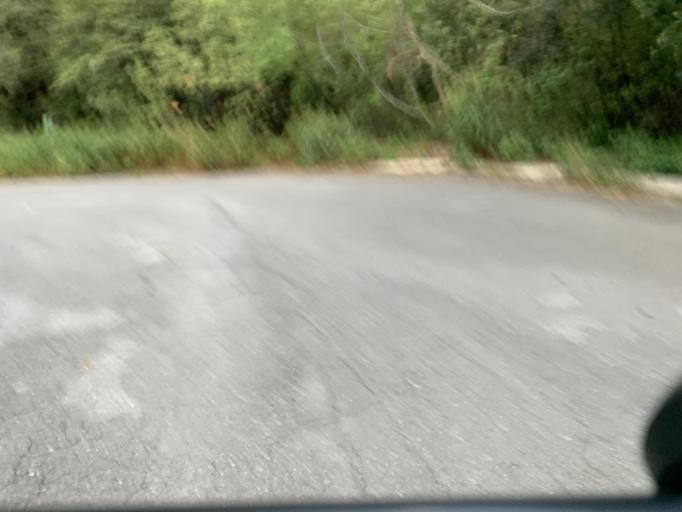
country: MX
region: Nuevo Leon
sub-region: Juarez
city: Bosques de San Pedro
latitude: 25.5114
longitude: -100.1799
